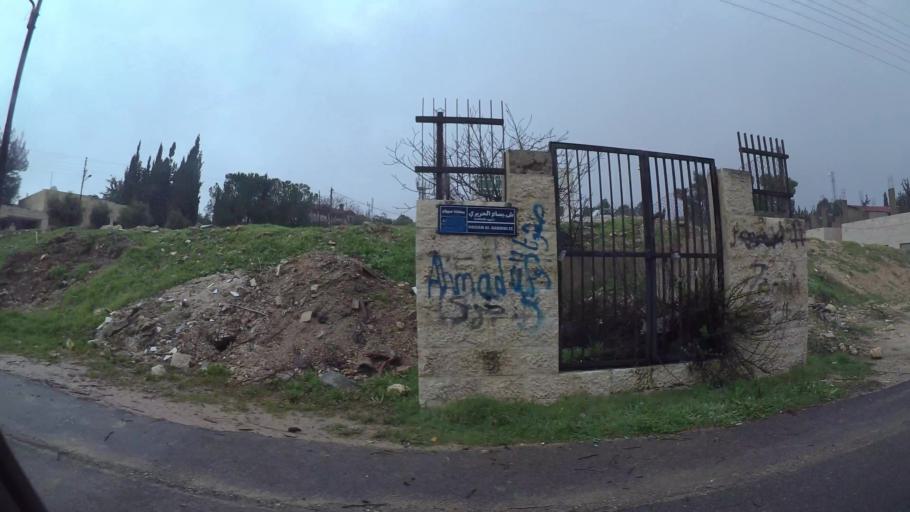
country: JO
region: Amman
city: Al Jubayhah
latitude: 32.0224
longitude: 35.8334
